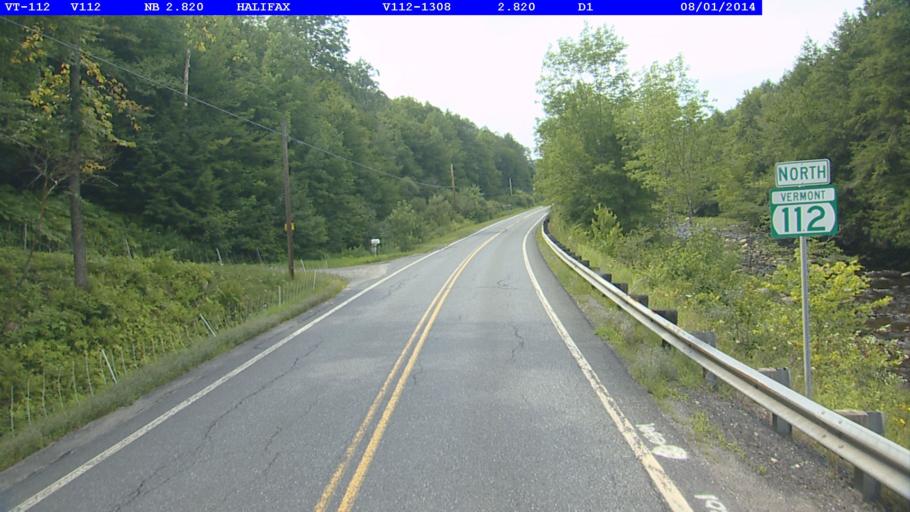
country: US
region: Massachusetts
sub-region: Franklin County
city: Colrain
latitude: 42.7584
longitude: -72.7618
